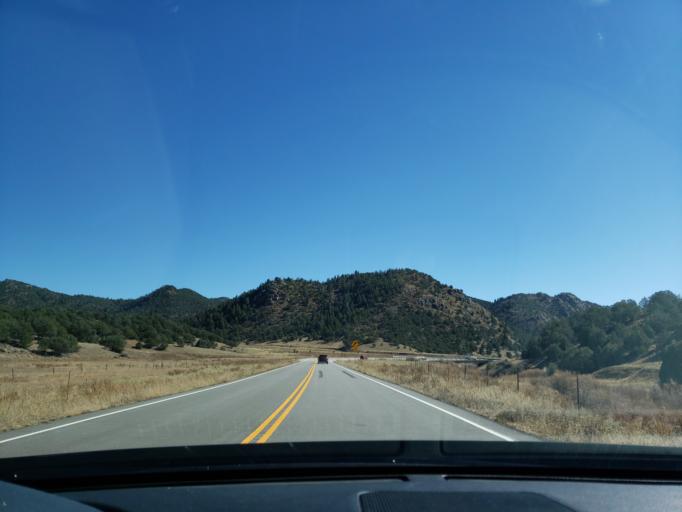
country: US
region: Colorado
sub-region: Fremont County
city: Canon City
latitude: 38.6186
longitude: -105.4482
